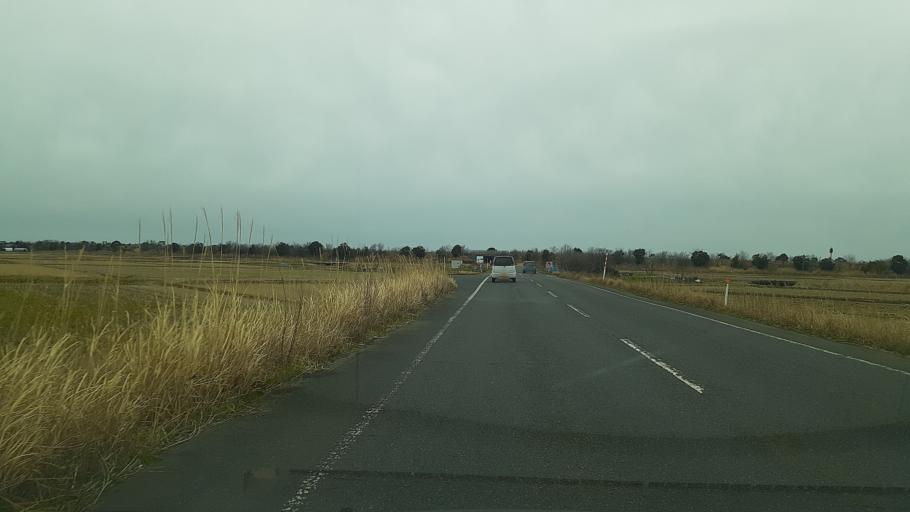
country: JP
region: Niigata
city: Niitsu-honcho
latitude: 37.8187
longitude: 139.0843
